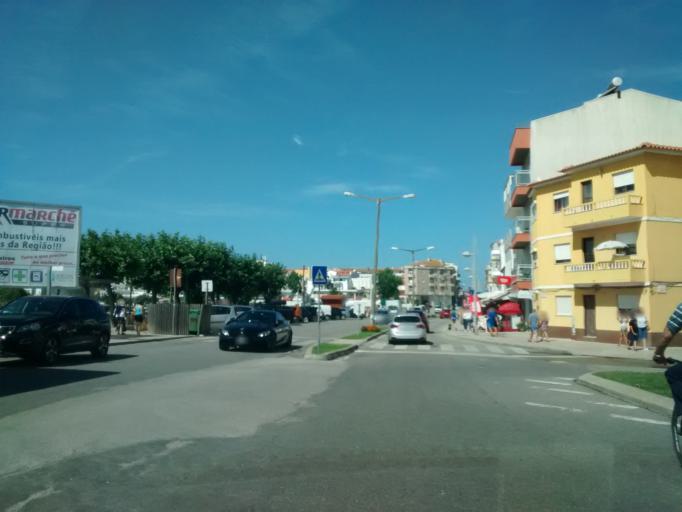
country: PT
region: Coimbra
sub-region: Mira
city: Mira
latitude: 40.4557
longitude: -8.7988
